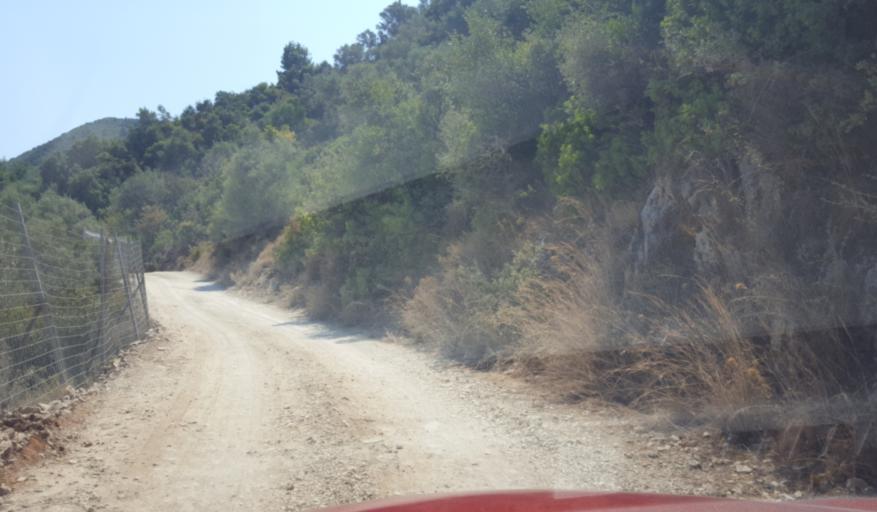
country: GR
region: Ionian Islands
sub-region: Lefkada
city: Nidri
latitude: 38.6678
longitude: 20.7119
